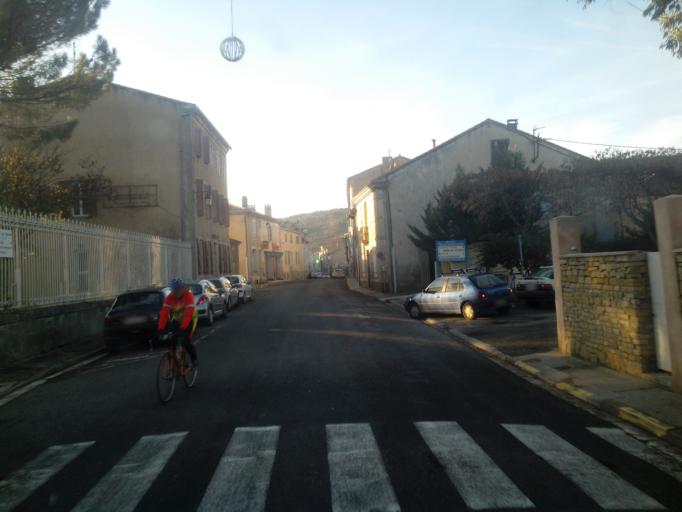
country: FR
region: Languedoc-Roussillon
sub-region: Departement de l'Aude
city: Esperaza
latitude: 42.9344
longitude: 2.2242
